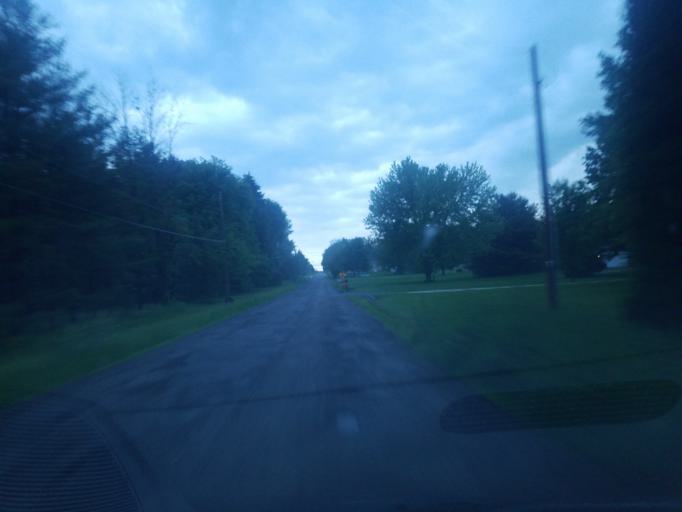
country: US
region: Ohio
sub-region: Mahoning County
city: Canfield
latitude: 40.9728
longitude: -80.7932
